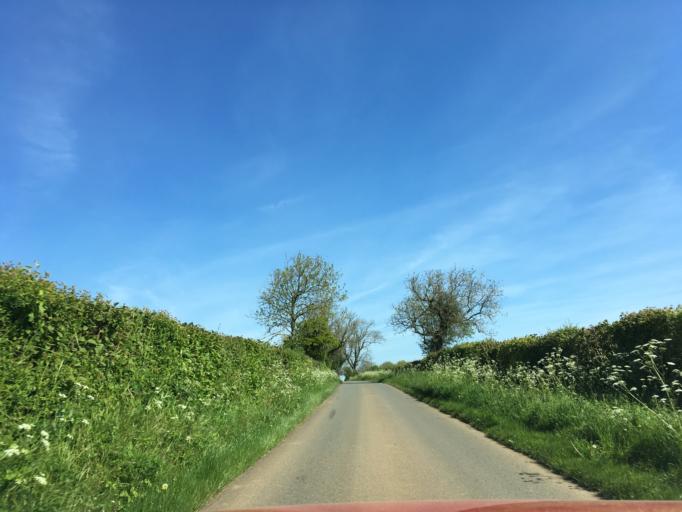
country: GB
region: England
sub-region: Wiltshire
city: Luckington
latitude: 51.5979
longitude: -2.2559
